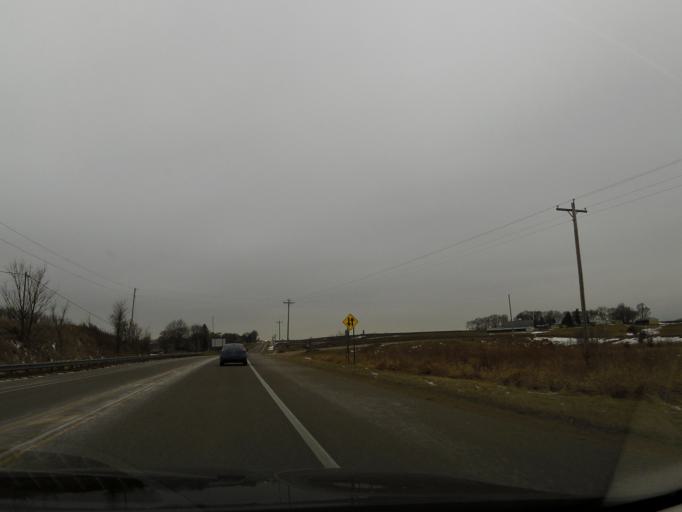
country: US
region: Minnesota
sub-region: Carver County
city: Carver
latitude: 44.7759
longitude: -93.6619
